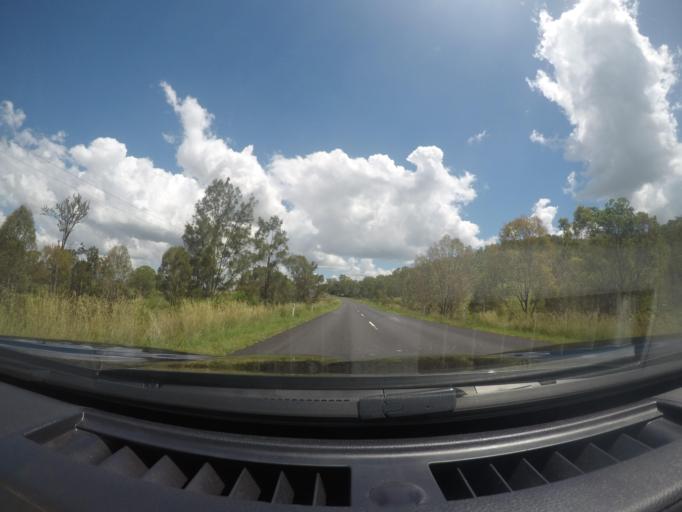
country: AU
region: Queensland
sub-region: Moreton Bay
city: Woodford
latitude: -27.1388
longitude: 152.5539
